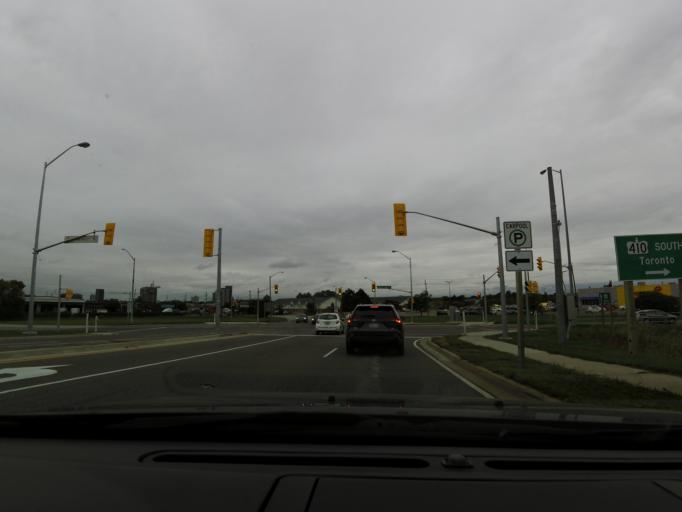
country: CA
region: Ontario
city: Brampton
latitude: 43.7013
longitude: -79.7350
